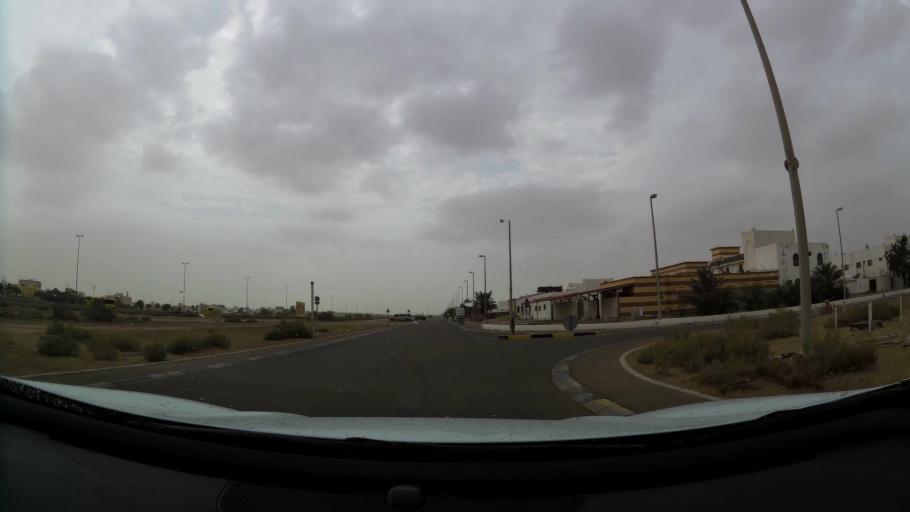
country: AE
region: Abu Dhabi
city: Abu Dhabi
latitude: 24.3583
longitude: 54.6561
